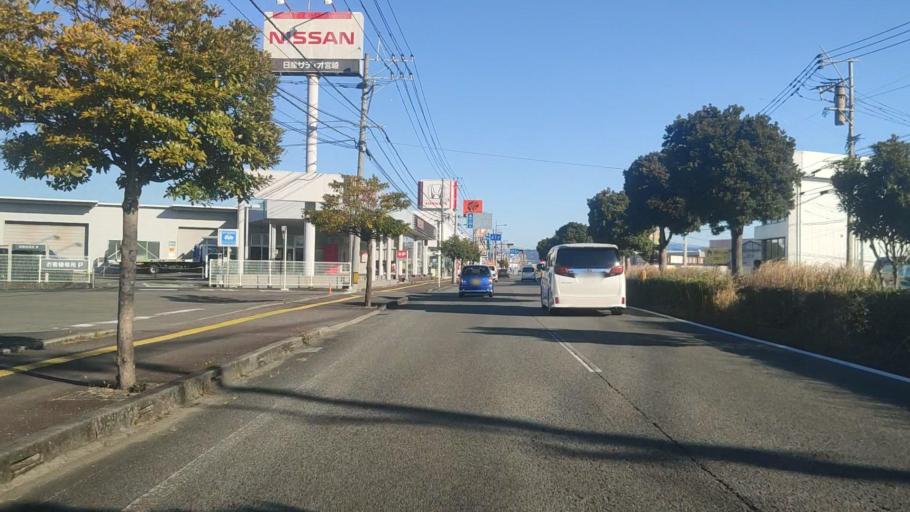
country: JP
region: Miyazaki
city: Nobeoka
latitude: 32.5598
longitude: 131.6805
